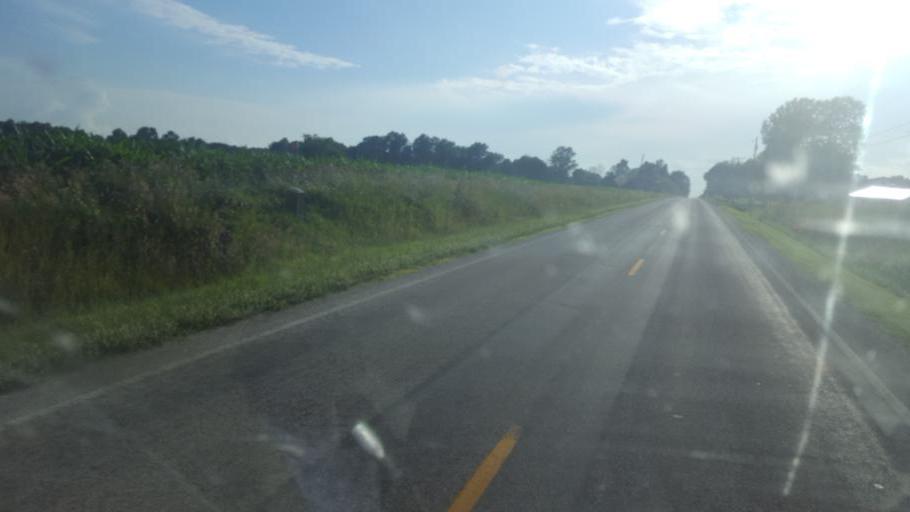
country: US
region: Ohio
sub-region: Ashland County
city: Ashland
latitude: 40.7727
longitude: -82.3085
